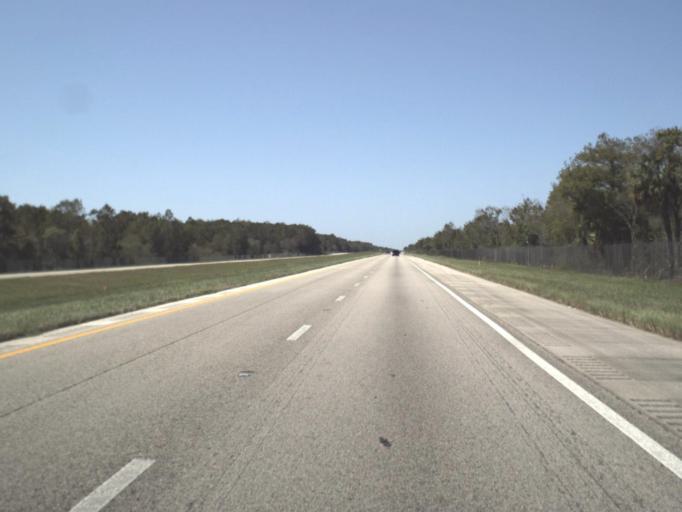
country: US
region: Florida
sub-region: Collier County
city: Orangetree
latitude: 26.1544
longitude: -81.3820
